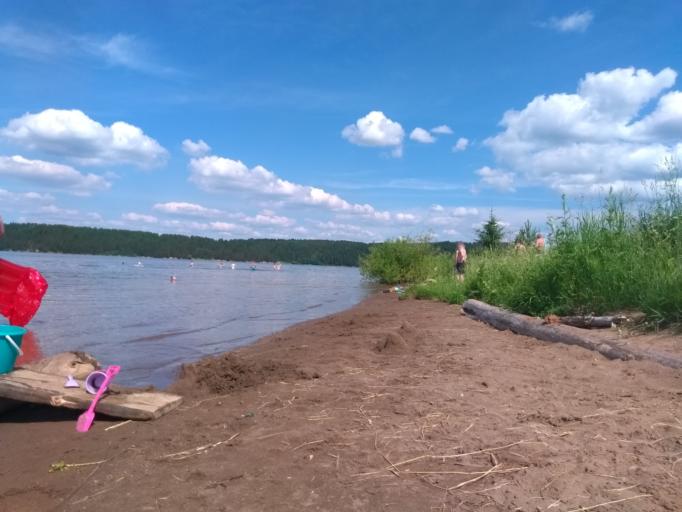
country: RU
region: Perm
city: Sylva
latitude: 57.8502
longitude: 56.7861
